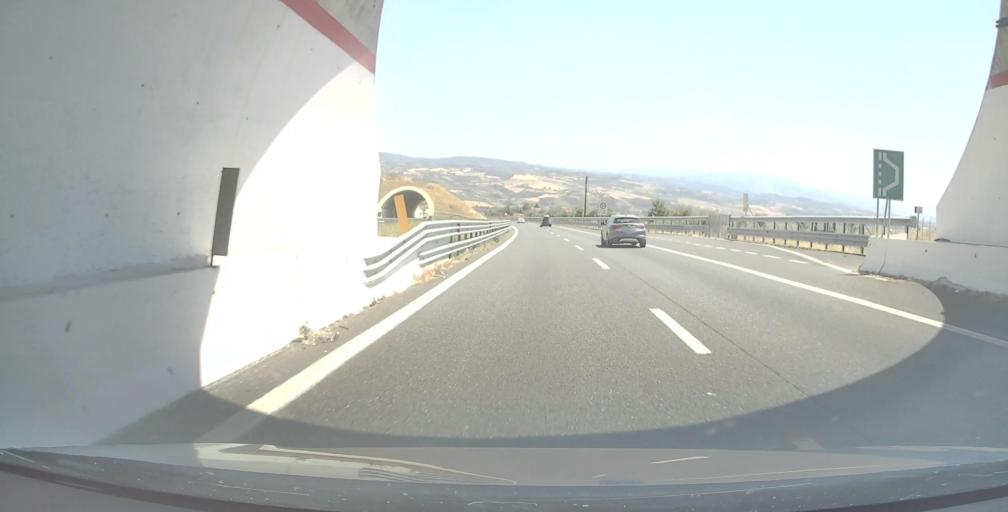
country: IT
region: Calabria
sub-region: Provincia di Cosenza
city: Tarsia
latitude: 39.6007
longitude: 16.2368
